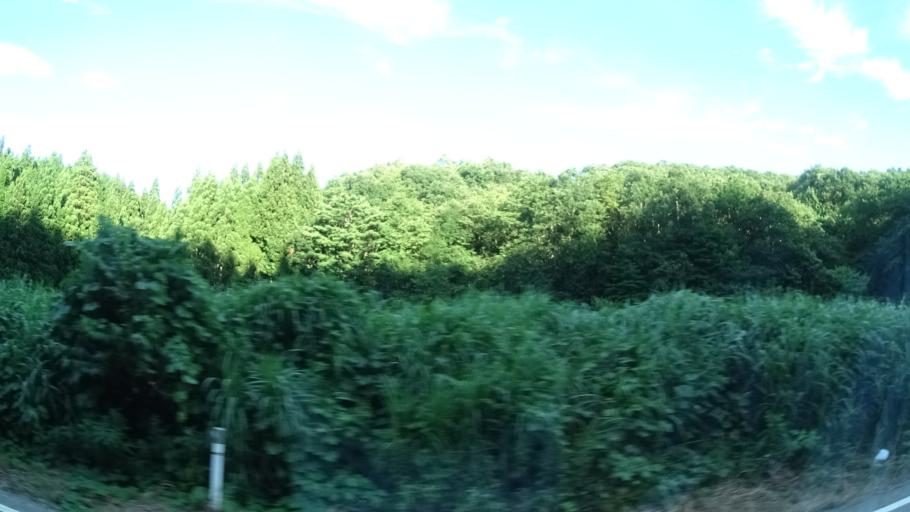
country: JP
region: Ishikawa
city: Nanao
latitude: 37.2682
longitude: 136.8844
